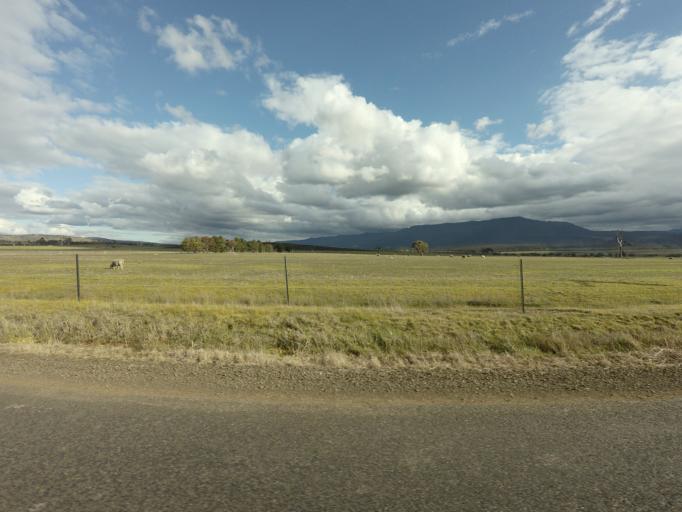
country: AU
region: Tasmania
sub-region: Northern Midlands
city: Longford
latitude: -41.8607
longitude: 147.2483
